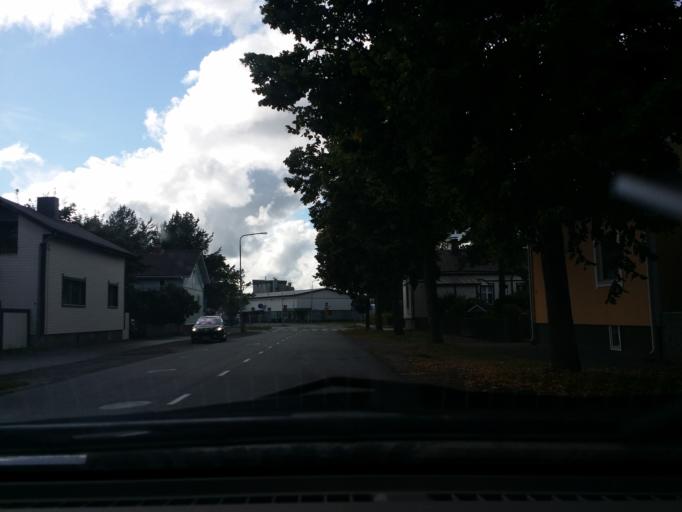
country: FI
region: Satakunta
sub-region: Pori
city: Pori
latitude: 61.4718
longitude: 21.8040
